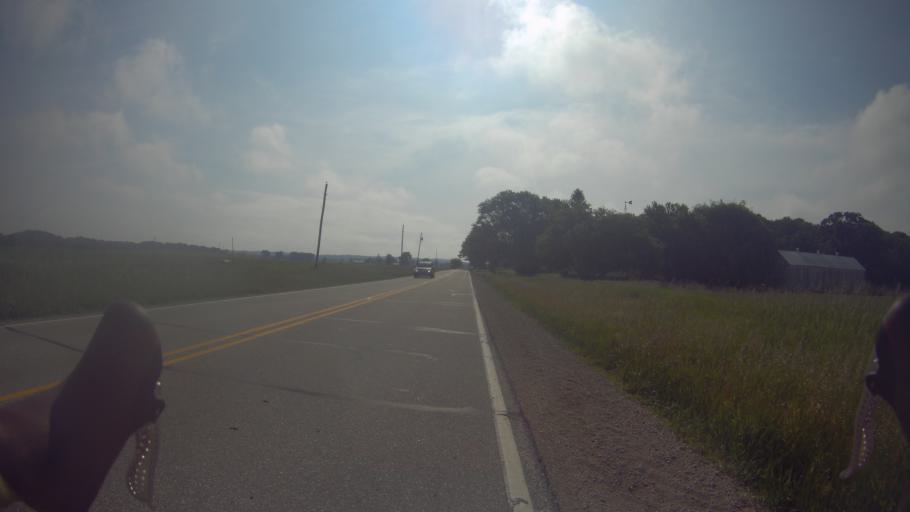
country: US
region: Wisconsin
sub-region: Dane County
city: McFarland
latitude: 43.0144
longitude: -89.2601
